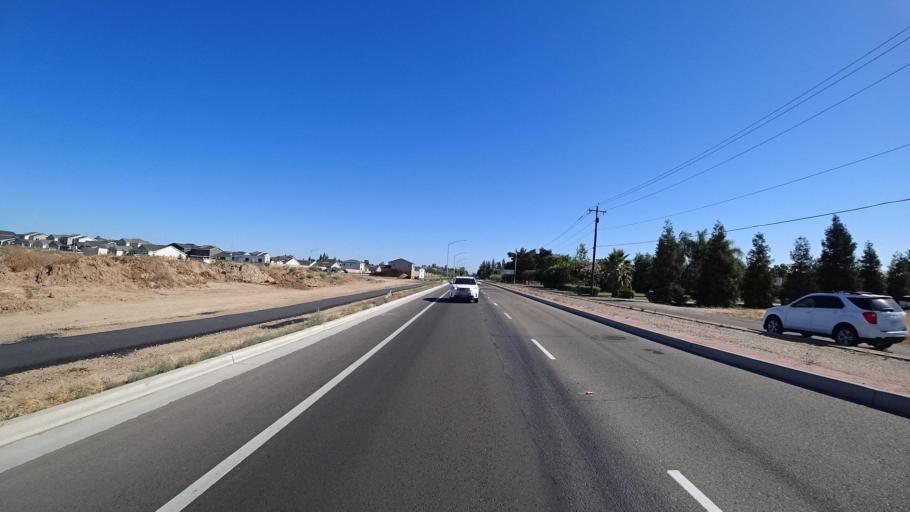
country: US
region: California
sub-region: Fresno County
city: Sunnyside
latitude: 36.7160
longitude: -119.6822
